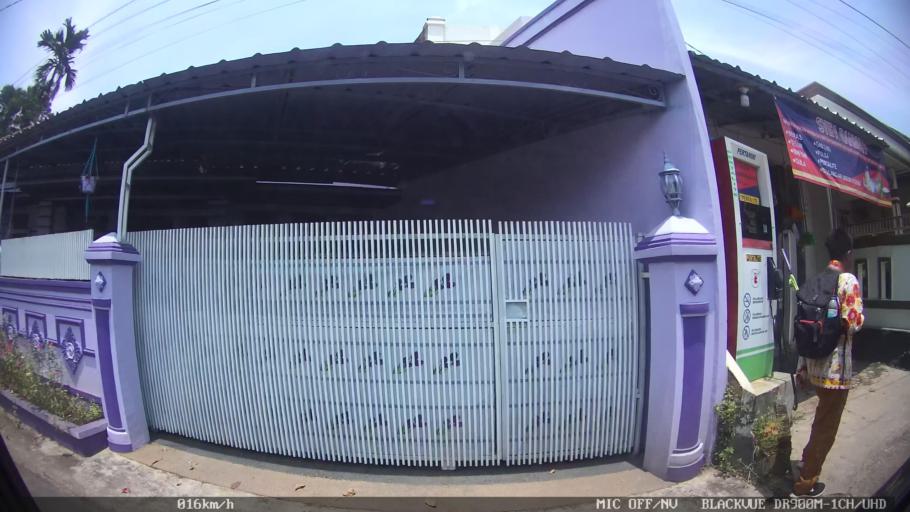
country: ID
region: Lampung
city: Bandarlampung
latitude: -5.4362
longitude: 105.2496
